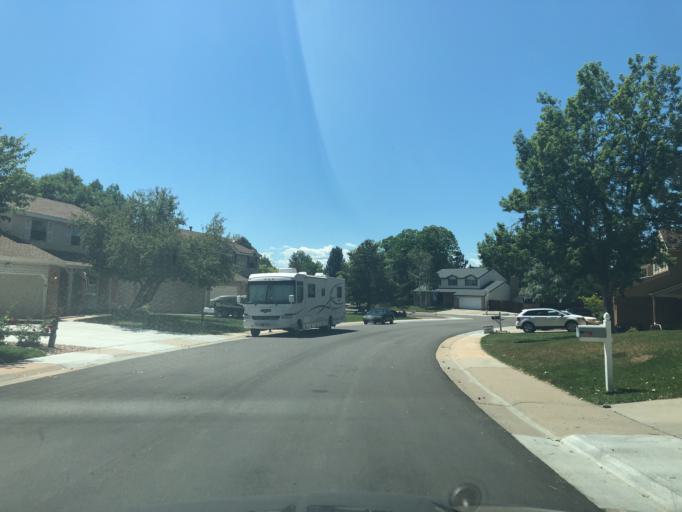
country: US
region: Colorado
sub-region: Arapahoe County
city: Dove Valley
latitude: 39.6153
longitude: -104.7863
